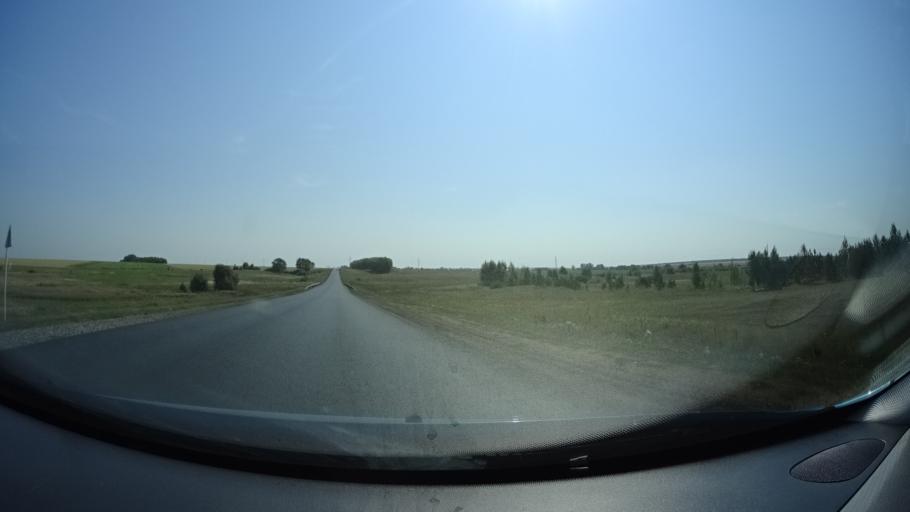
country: RU
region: Bashkortostan
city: Kabakovo
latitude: 54.4380
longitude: 56.0038
